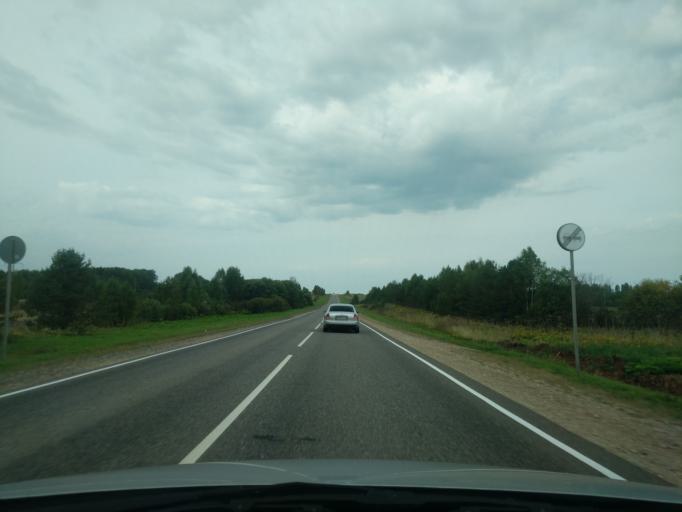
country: RU
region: Kirov
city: Mirnyy
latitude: 58.2727
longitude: 47.7845
